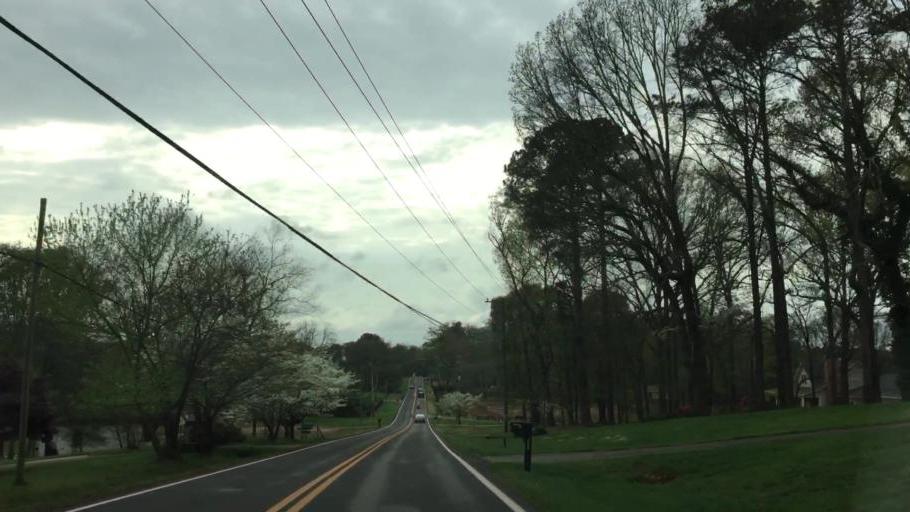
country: US
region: Georgia
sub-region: Fulton County
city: Milton
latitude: 34.1974
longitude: -84.3531
